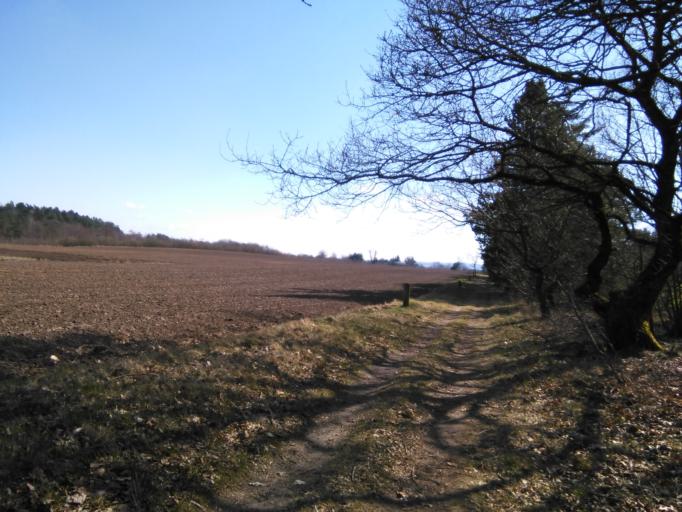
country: DK
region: Central Jutland
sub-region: Skanderborg Kommune
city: Ry
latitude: 56.0563
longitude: 9.7435
